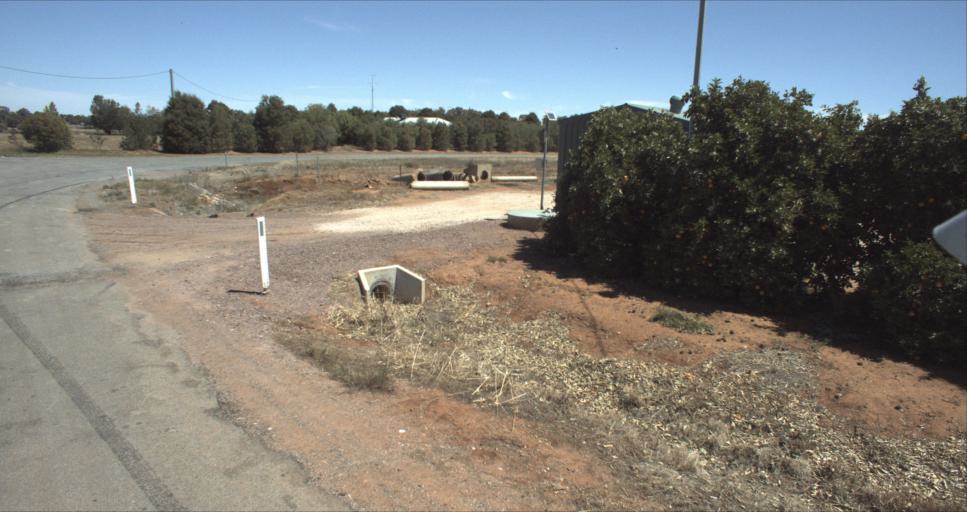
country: AU
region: New South Wales
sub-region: Leeton
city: Leeton
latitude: -34.5339
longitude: 146.3285
